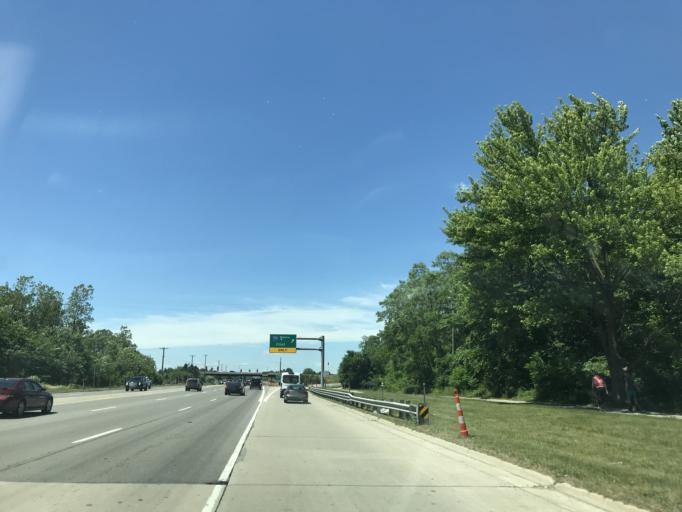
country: US
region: Michigan
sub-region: Wayne County
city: Westland
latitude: 42.3234
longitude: -83.4378
